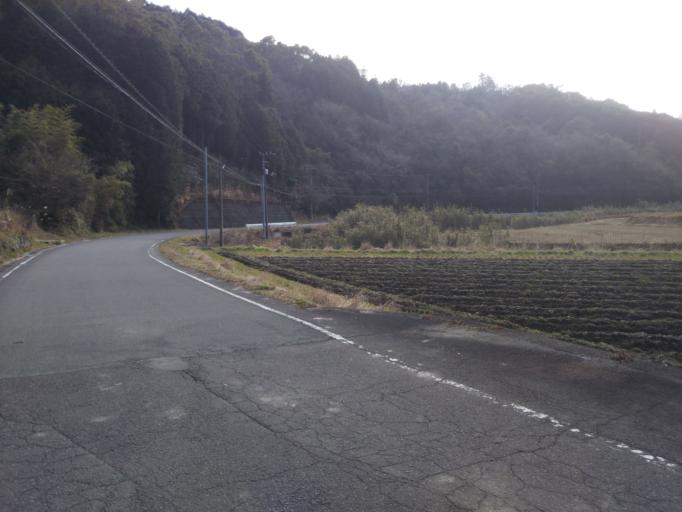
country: JP
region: Kochi
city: Nakamura
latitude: 33.0384
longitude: 132.9776
